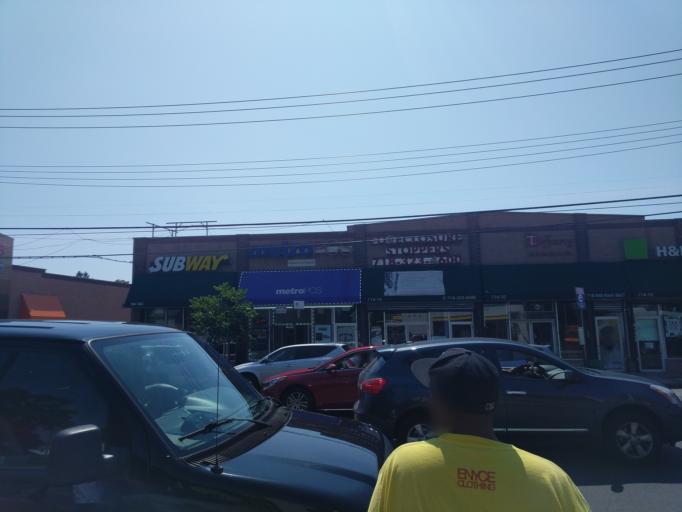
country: US
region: New York
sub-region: Queens County
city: Jamaica
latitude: 40.6860
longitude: -73.7936
